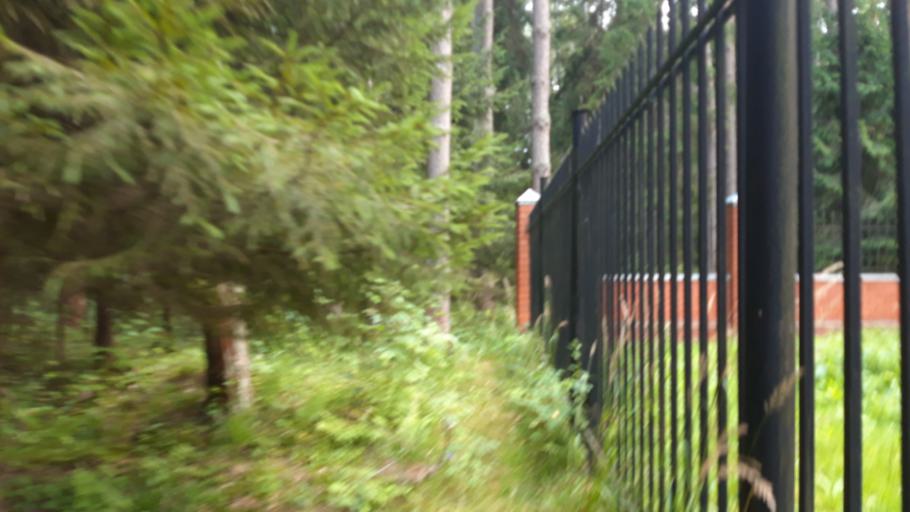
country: RU
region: Tverskaya
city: Konakovo
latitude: 56.6913
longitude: 36.7211
